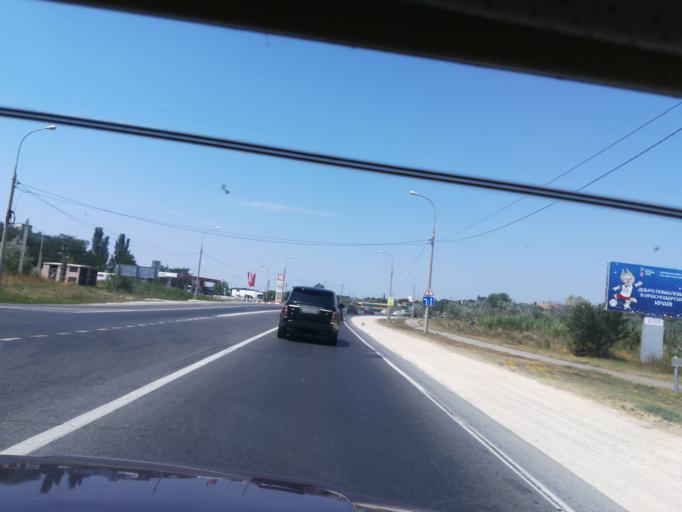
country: RU
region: Krasnodarskiy
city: Tsibanobalka
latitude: 44.9406
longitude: 37.3189
